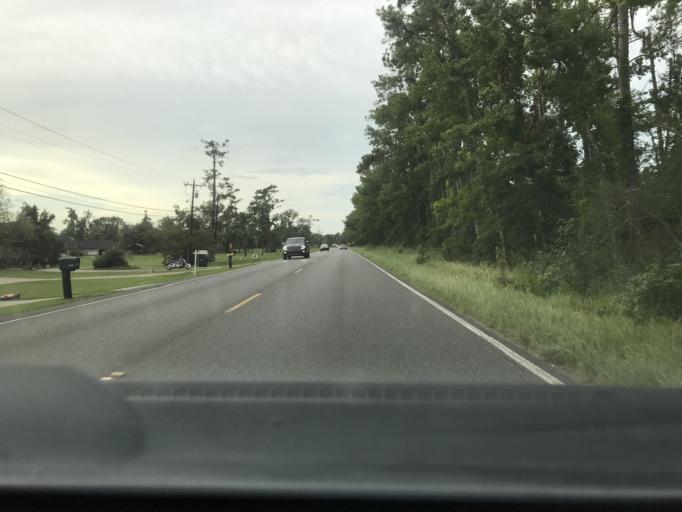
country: US
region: Louisiana
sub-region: Calcasieu Parish
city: Westlake
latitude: 30.2904
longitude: -93.2497
